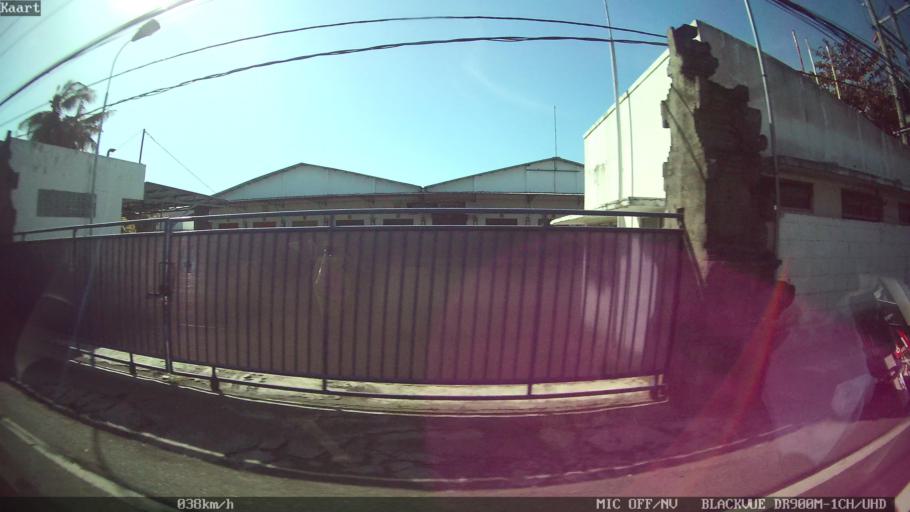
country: ID
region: Bali
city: Banjar Kertasari
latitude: -8.6178
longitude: 115.1934
